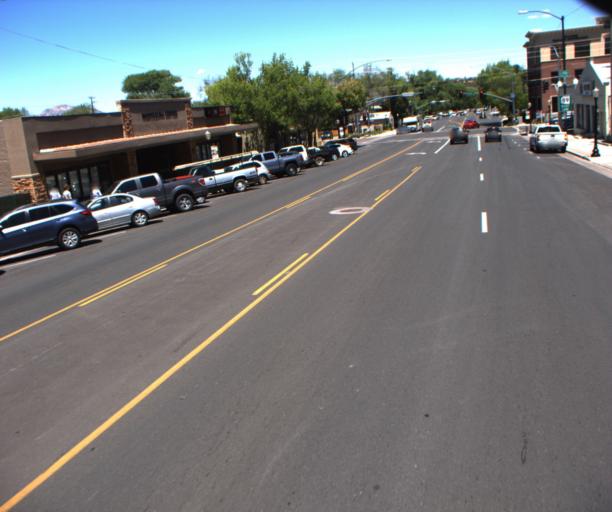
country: US
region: Arizona
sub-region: Yavapai County
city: Prescott
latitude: 34.5430
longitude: -112.4700
